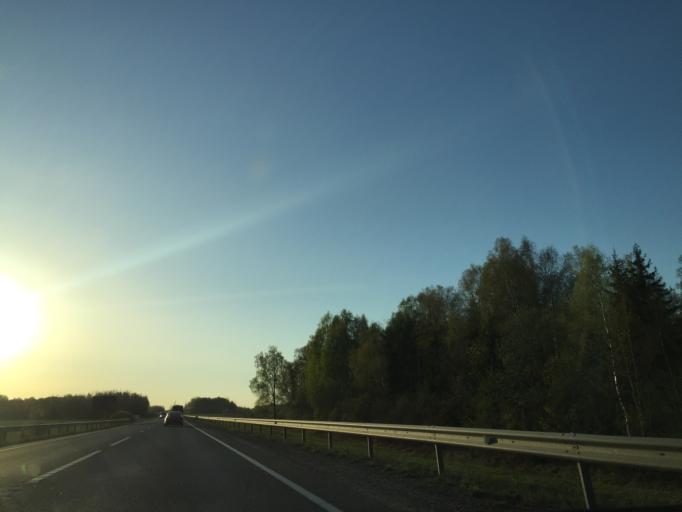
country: LV
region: Ogre
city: Jumprava
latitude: 56.7855
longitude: 25.0069
